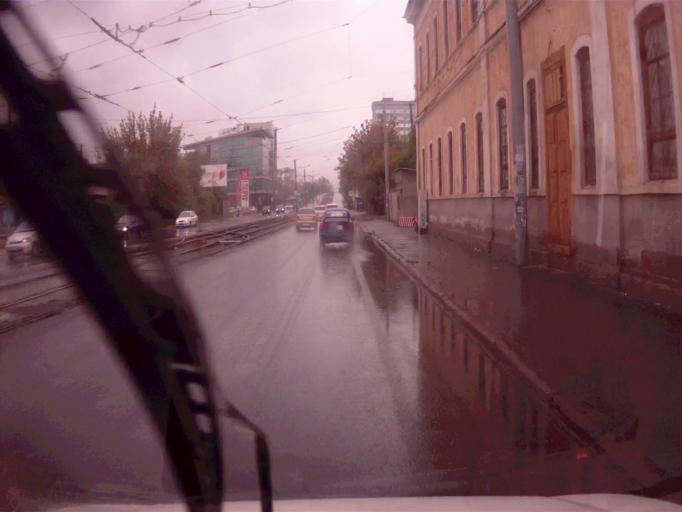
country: RU
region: Chelyabinsk
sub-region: Gorod Chelyabinsk
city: Chelyabinsk
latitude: 55.1682
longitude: 61.4158
